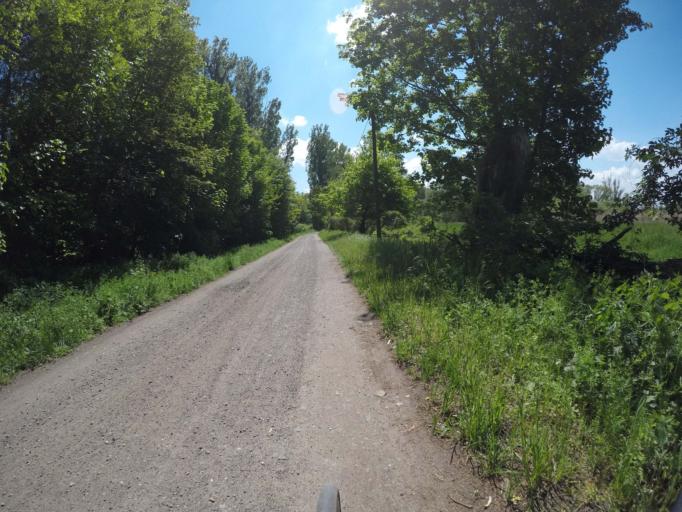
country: DE
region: Brandenburg
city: Werder
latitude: 52.4231
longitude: 12.9418
